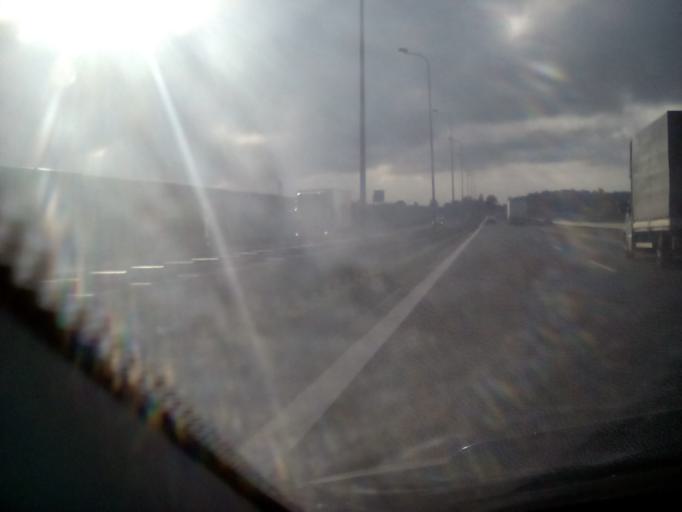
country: PL
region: Masovian Voivodeship
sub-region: Powiat bialobrzeski
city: Promna
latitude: 51.6916
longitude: 20.9333
